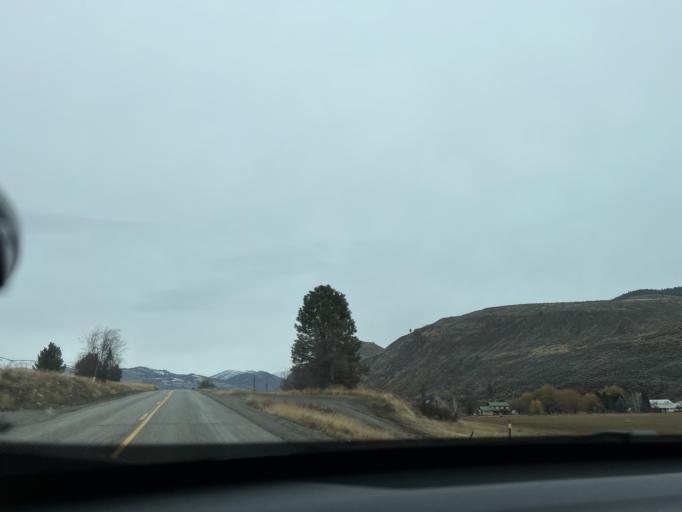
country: US
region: Washington
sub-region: Okanogan County
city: Brewster
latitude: 48.5119
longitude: -120.1742
